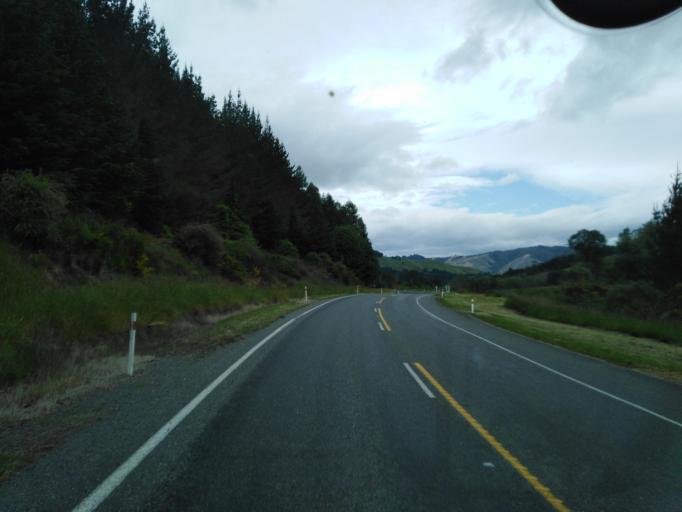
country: NZ
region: Tasman
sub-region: Tasman District
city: Wakefield
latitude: -41.4756
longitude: 172.8525
